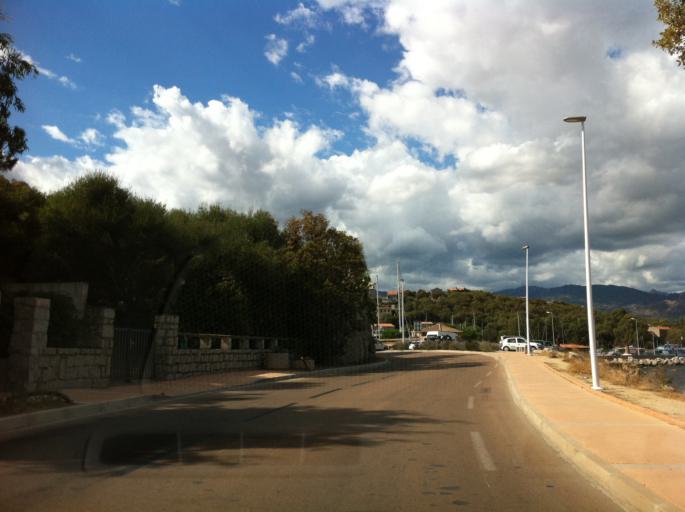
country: FR
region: Corsica
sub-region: Departement de la Corse-du-Sud
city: Porto-Vecchio
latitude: 41.5886
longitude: 9.2872
